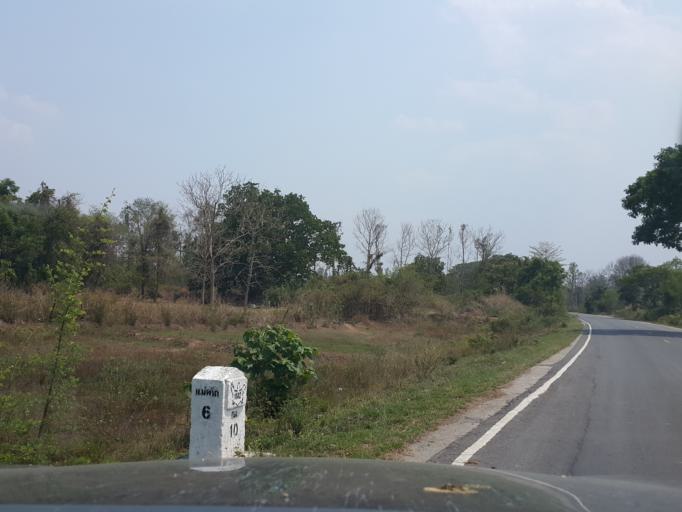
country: TH
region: Lampang
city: Mae Phrik
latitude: 17.4957
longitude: 99.1262
